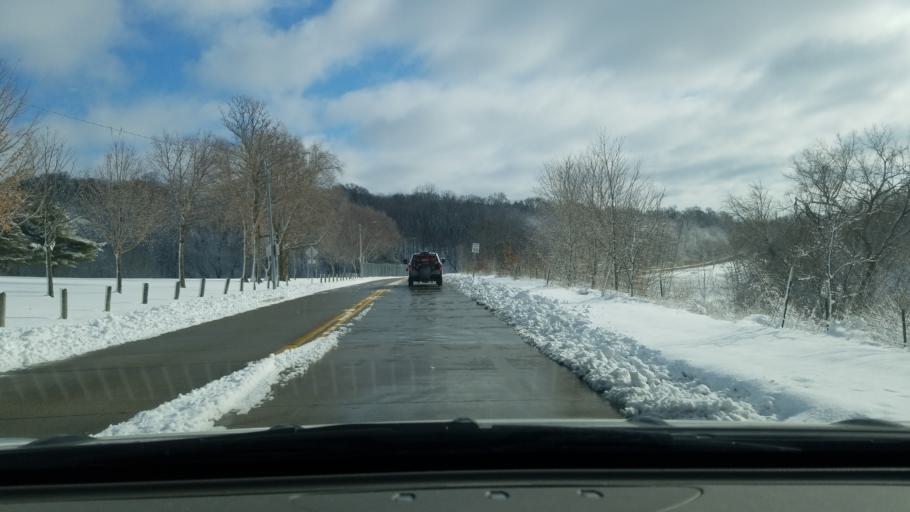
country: US
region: Nebraska
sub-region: Douglas County
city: Omaha
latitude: 41.2200
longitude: -95.9380
